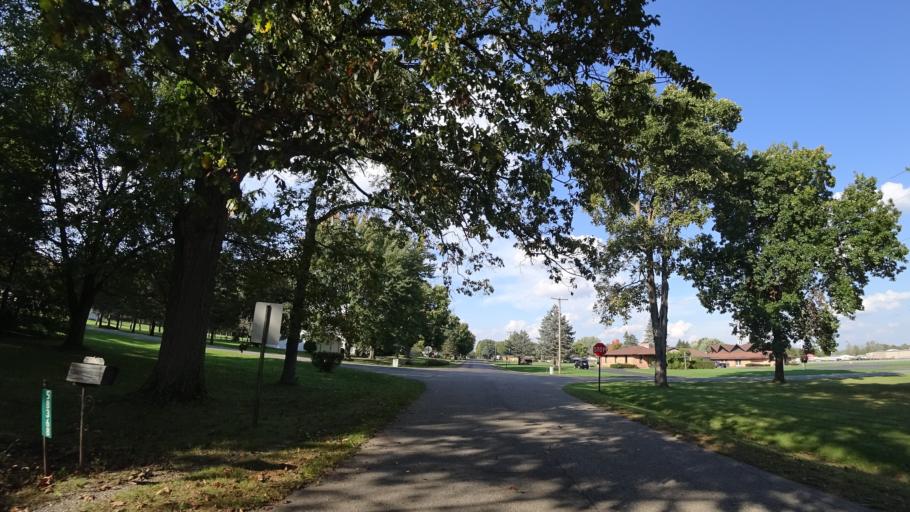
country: US
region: Michigan
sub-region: Saint Joseph County
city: Three Rivers
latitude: 41.9488
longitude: -85.6516
